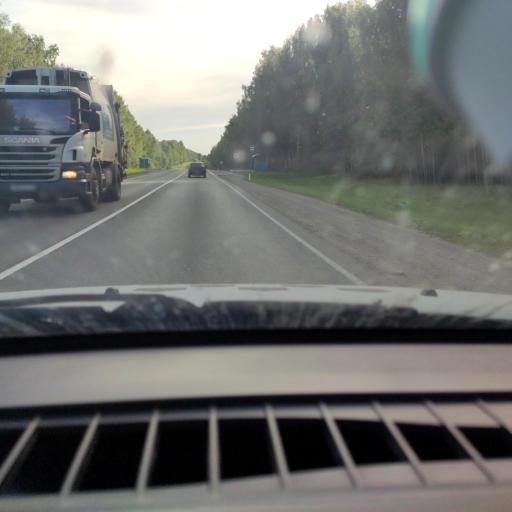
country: RU
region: Kirov
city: Vakhrushi
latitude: 58.6471
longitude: 49.8616
